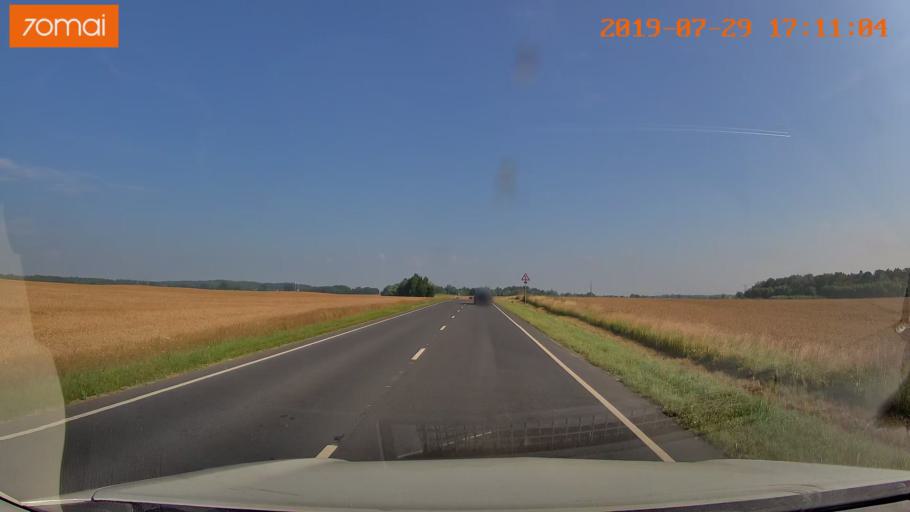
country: RU
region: Kaliningrad
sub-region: Gorod Kaliningrad
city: Kaliningrad
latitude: 54.7977
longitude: 20.3759
